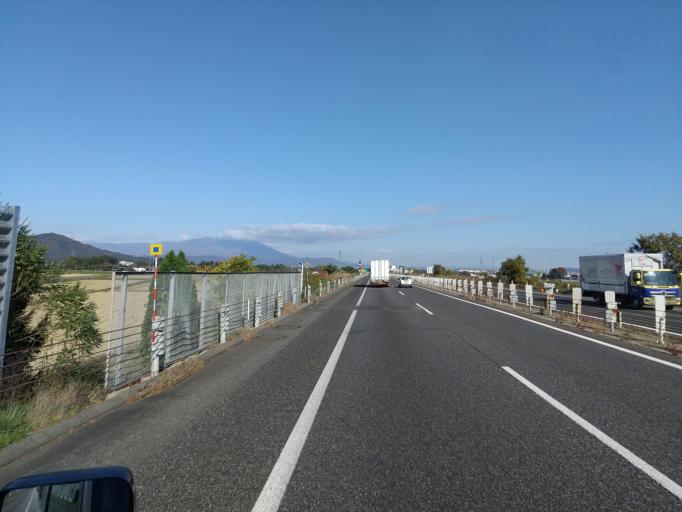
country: JP
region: Iwate
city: Morioka-shi
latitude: 39.6411
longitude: 141.1254
